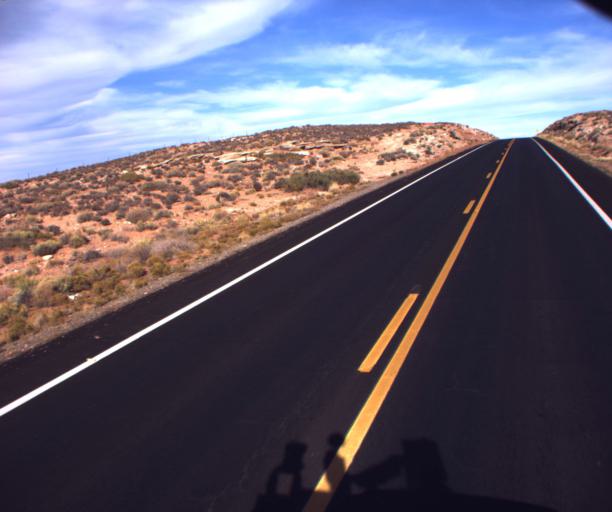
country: US
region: Arizona
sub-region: Apache County
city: Many Farms
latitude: 36.9509
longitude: -109.5170
